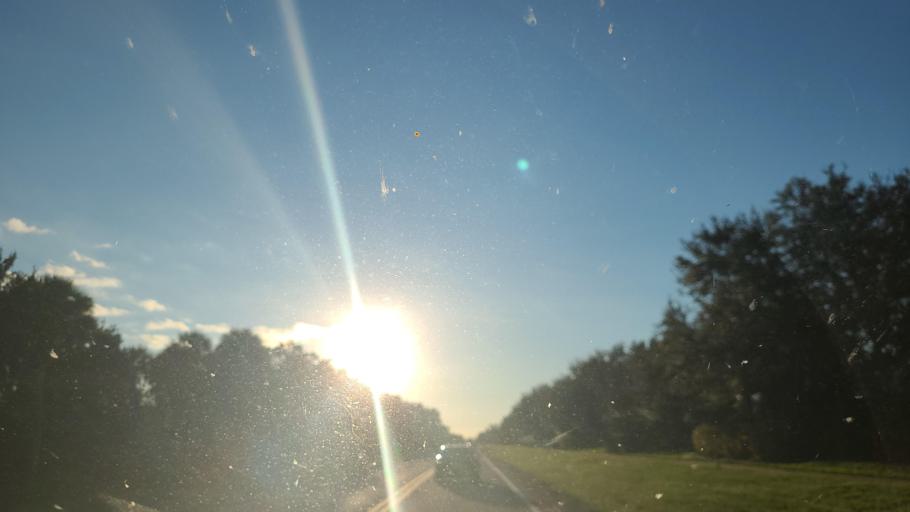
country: US
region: Florida
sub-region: Indian River County
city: Vero Beach South
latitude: 27.5946
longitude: -80.4382
